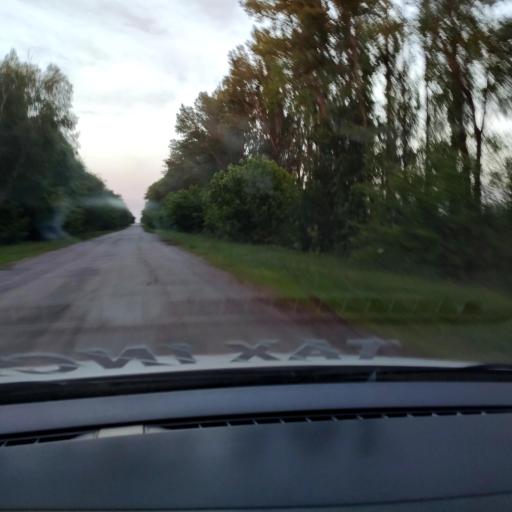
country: RU
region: Voronezj
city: Maslovka
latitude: 51.4429
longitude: 39.2671
